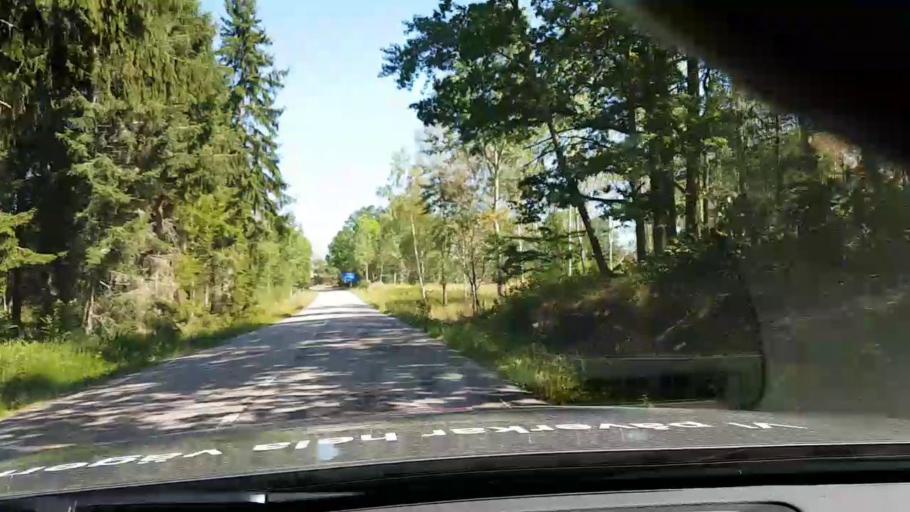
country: SE
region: Kalmar
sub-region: Hultsfreds Kommun
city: Virserum
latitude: 57.1329
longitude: 15.6586
